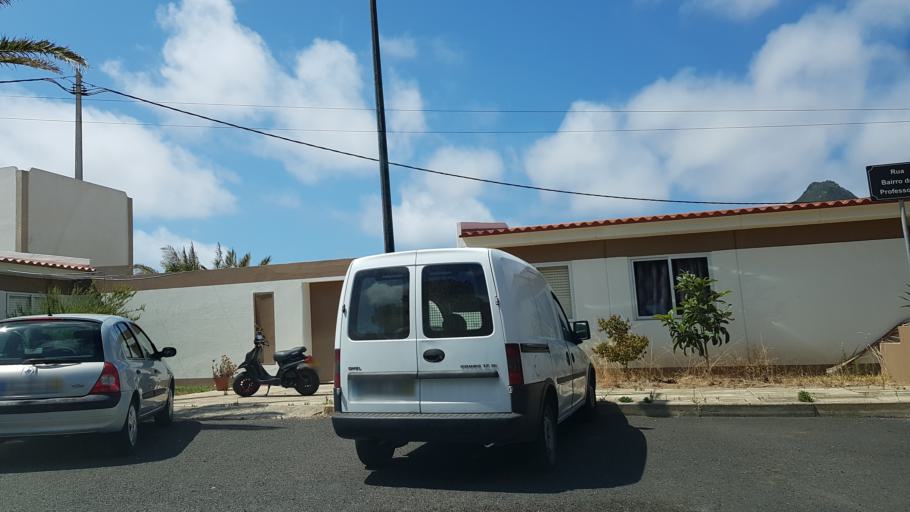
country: PT
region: Madeira
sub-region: Porto Santo
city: Vila de Porto Santo
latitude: 33.0621
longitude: -16.3394
